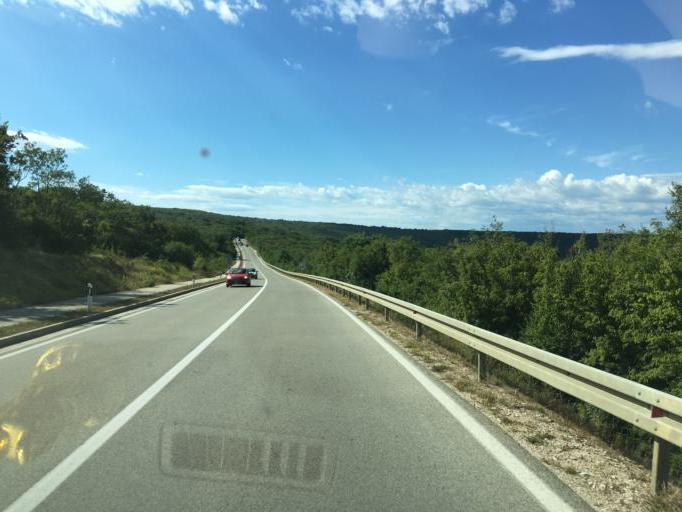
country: HR
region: Primorsko-Goranska
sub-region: Grad Krk
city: Krk
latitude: 45.0685
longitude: 14.5554
